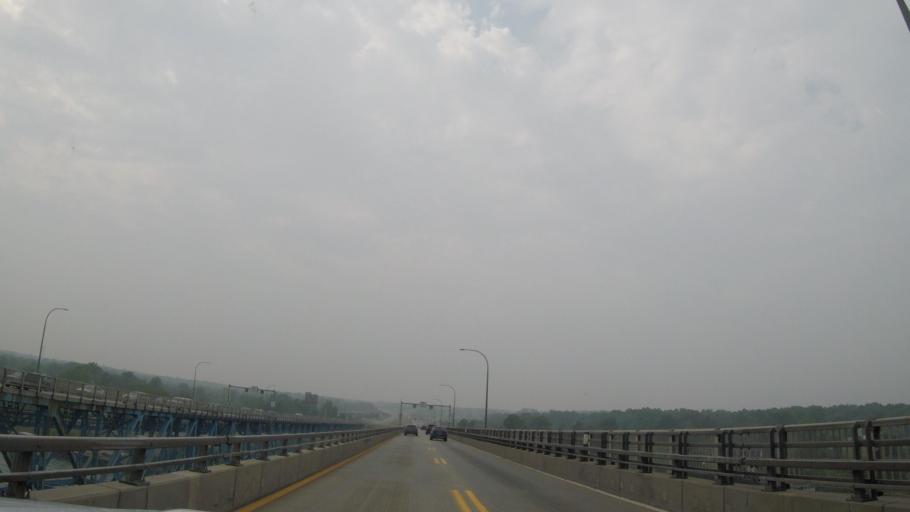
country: US
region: New York
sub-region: Erie County
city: Grandyle Village
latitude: 42.9991
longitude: -78.9374
